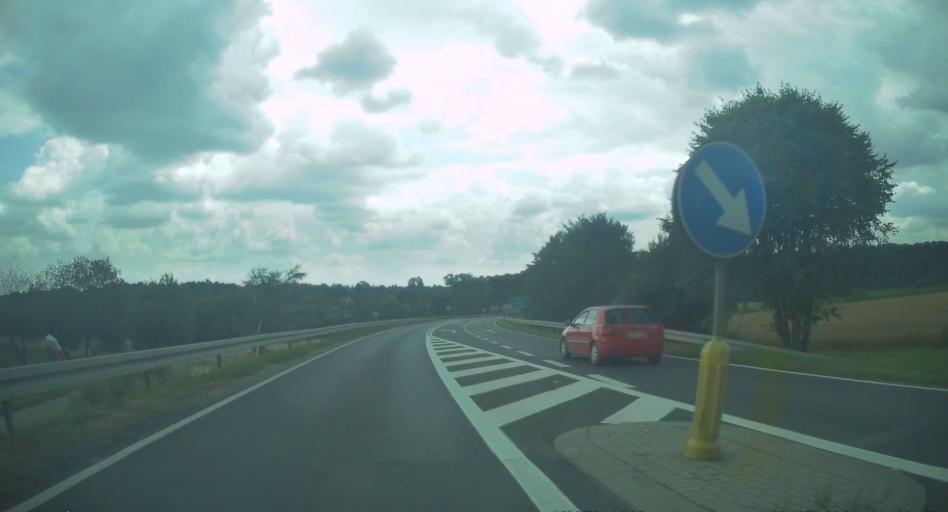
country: PL
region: Opole Voivodeship
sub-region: Powiat prudnicki
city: Laka Prudnicka
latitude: 50.4087
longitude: 17.5075
